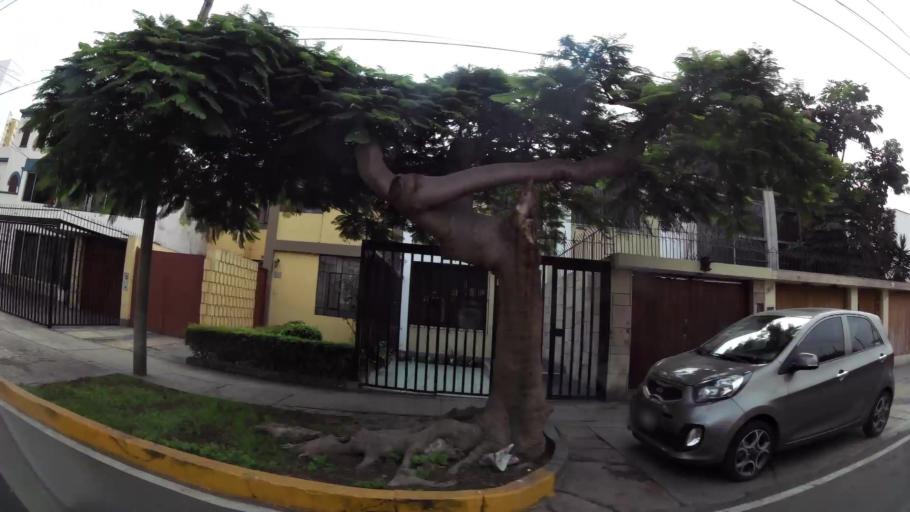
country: PE
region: Lima
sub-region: Lima
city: San Isidro
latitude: -12.0812
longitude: -77.0504
